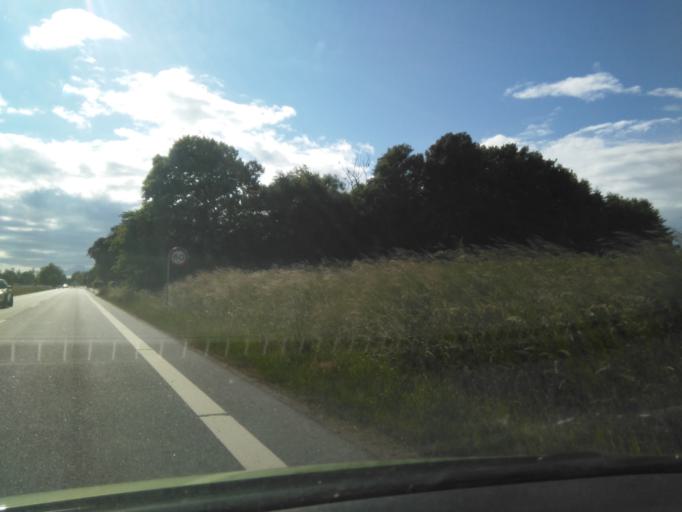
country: DK
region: Capital Region
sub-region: Bornholm Kommune
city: Akirkeby
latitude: 55.1385
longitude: 15.0246
